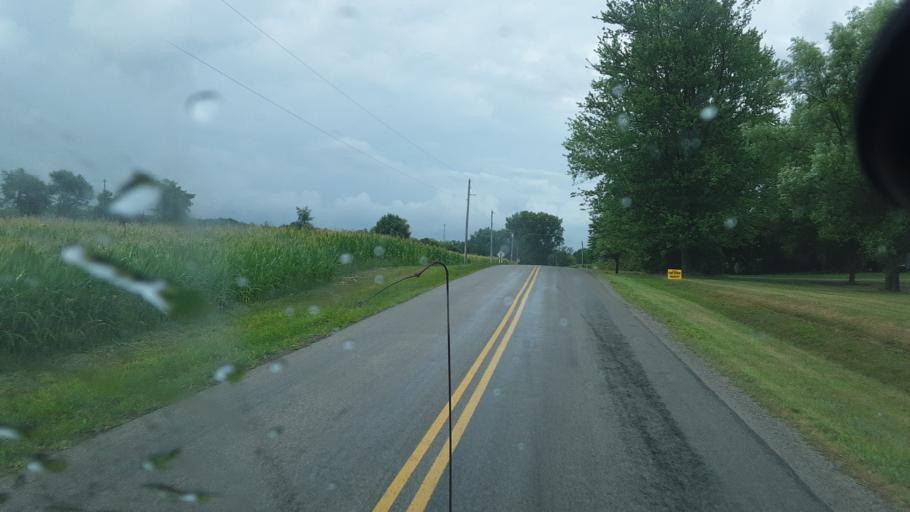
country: US
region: Indiana
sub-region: Steuben County
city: Hamilton
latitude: 41.6421
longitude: -84.7911
